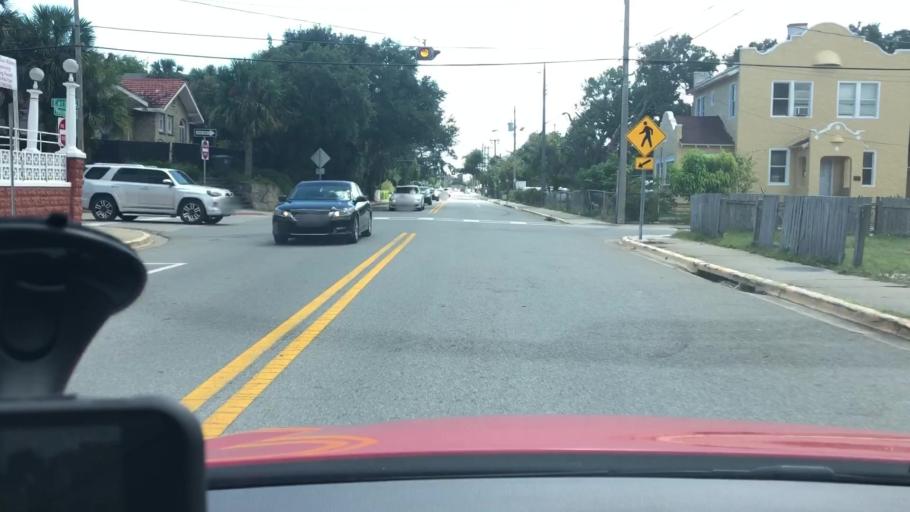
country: US
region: Florida
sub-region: Volusia County
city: Daytona Beach
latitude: 29.2283
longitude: -81.0146
